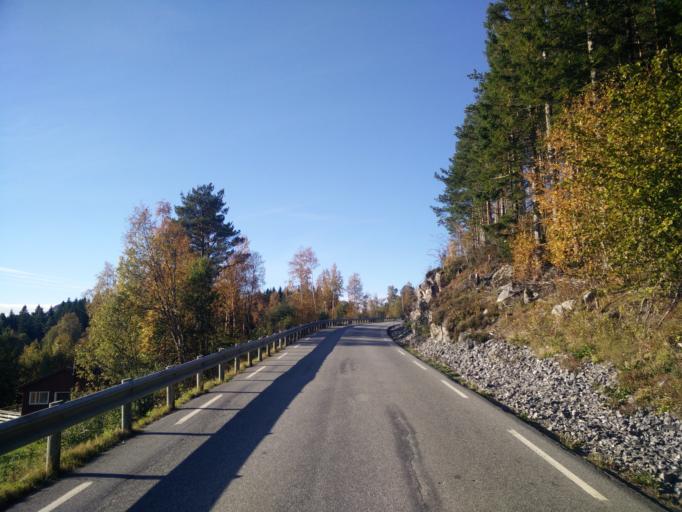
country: NO
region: More og Romsdal
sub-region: Halsa
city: Liaboen
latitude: 63.1170
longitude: 8.3129
